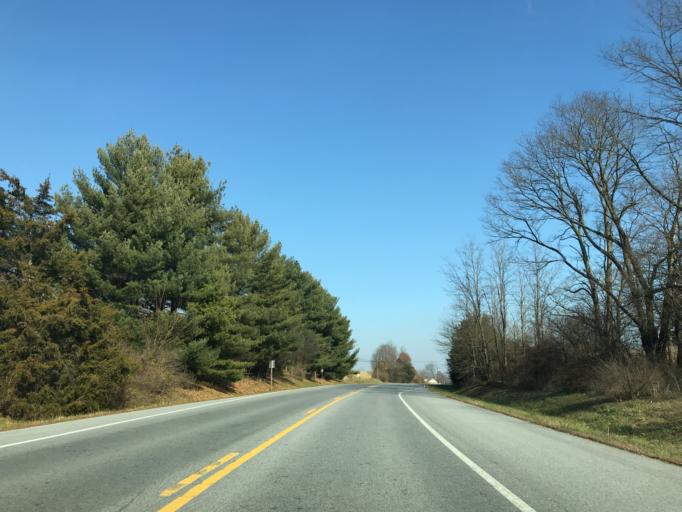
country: US
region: Maryland
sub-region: Carroll County
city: Taneytown
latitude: 39.6933
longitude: -77.1438
